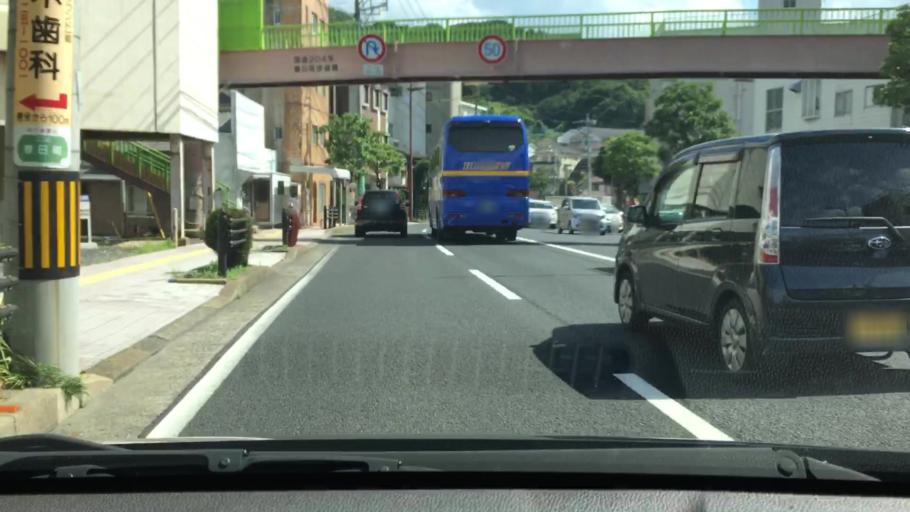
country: JP
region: Nagasaki
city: Sasebo
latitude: 33.1982
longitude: 129.7225
